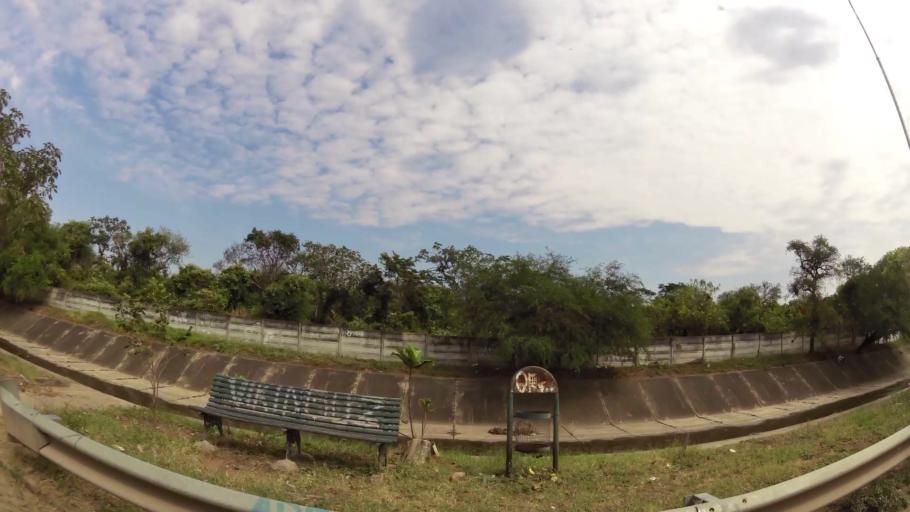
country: BO
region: Santa Cruz
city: Santa Cruz de la Sierra
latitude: -17.7316
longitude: -63.1818
